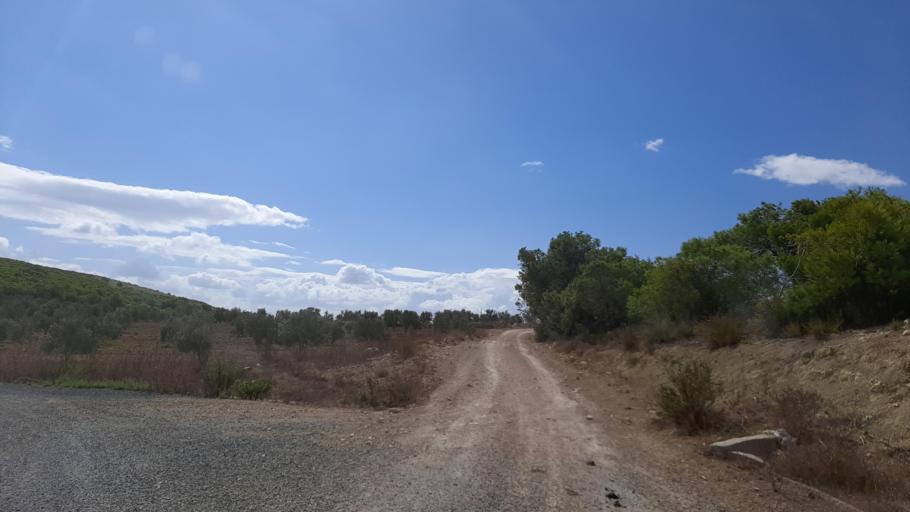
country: TN
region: Zaghwan
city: Zaghouan
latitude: 36.5124
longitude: 10.1833
